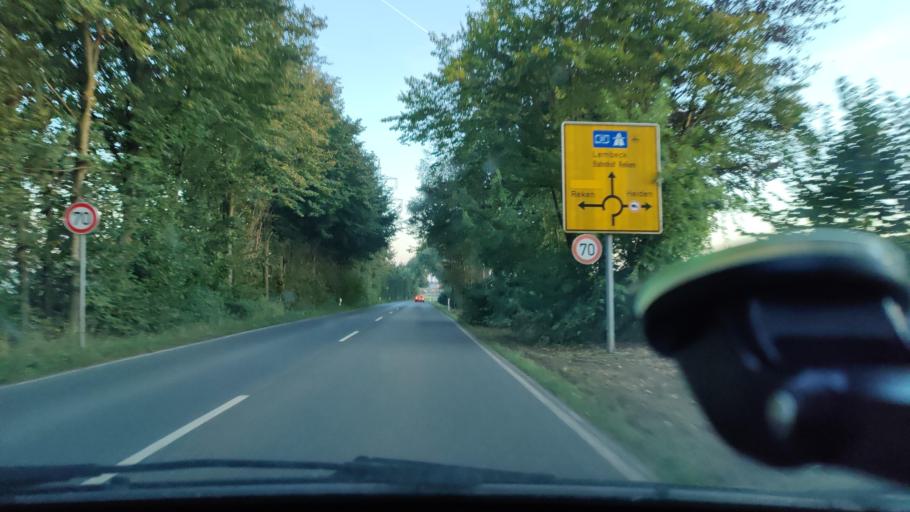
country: DE
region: North Rhine-Westphalia
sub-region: Regierungsbezirk Munster
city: Heiden
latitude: 51.8269
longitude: 6.9499
